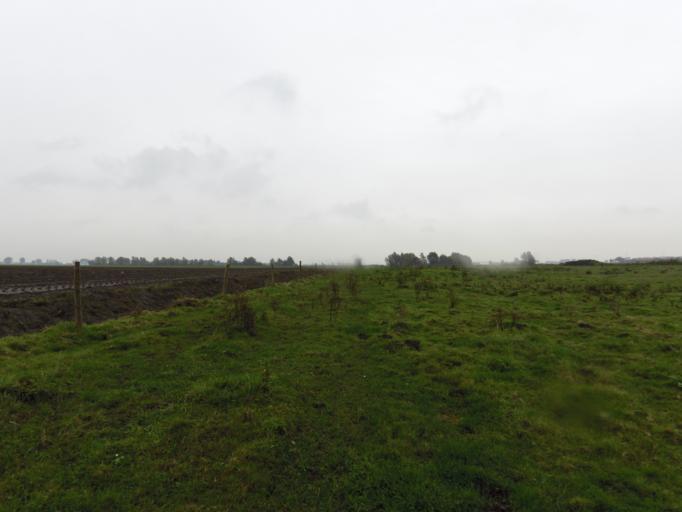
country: NL
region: North Brabant
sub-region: Gemeente Steenbergen
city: Dinteloord
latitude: 51.6783
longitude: 4.2821
